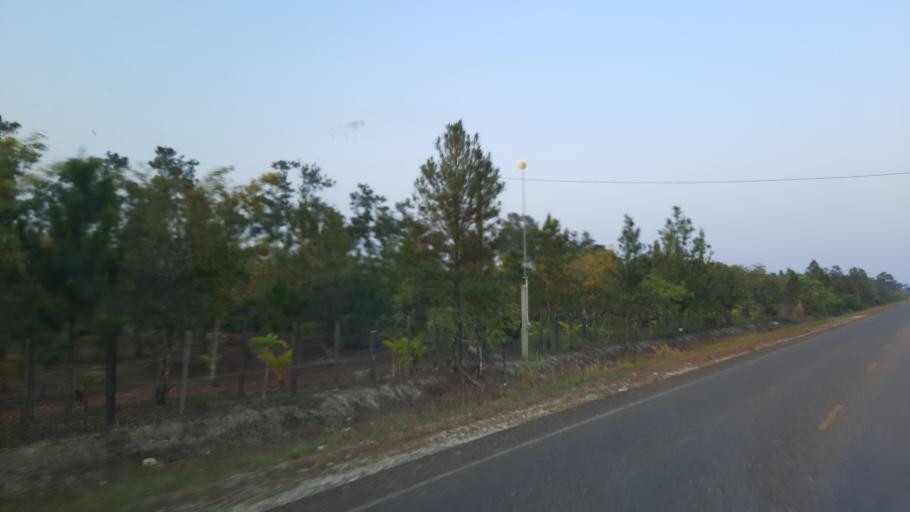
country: BZ
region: Stann Creek
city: Placencia
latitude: 16.5312
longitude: -88.4546
